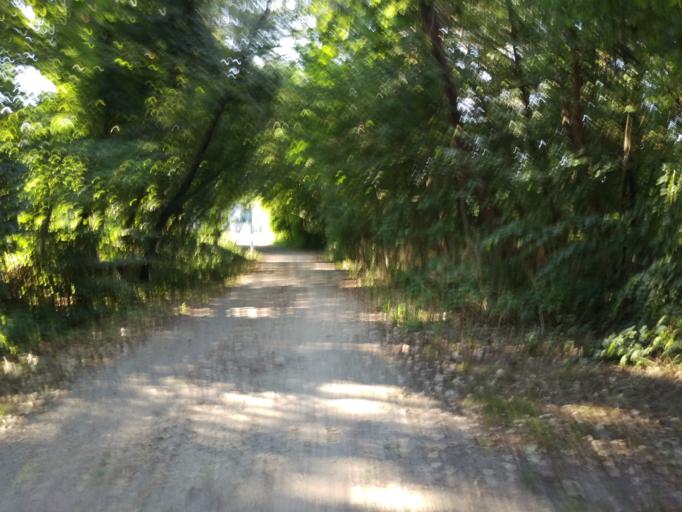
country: AT
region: Styria
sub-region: Graz Stadt
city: Goesting
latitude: 47.0986
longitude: 15.4125
